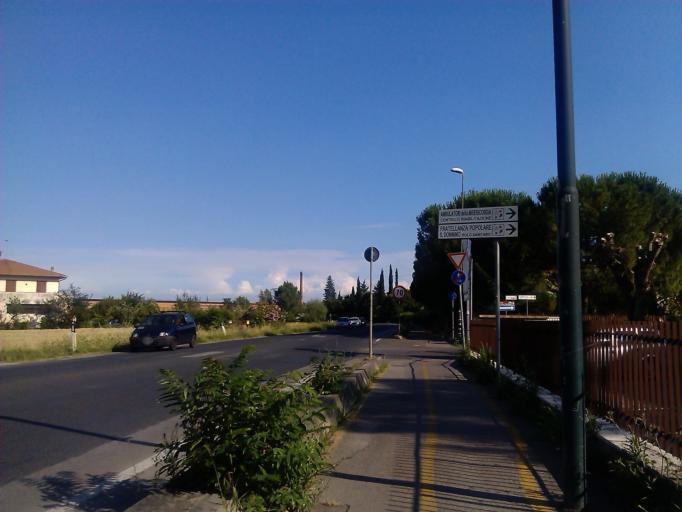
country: IT
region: Tuscany
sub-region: Province of Florence
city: Campi Bisenzio
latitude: 43.8202
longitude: 11.1484
